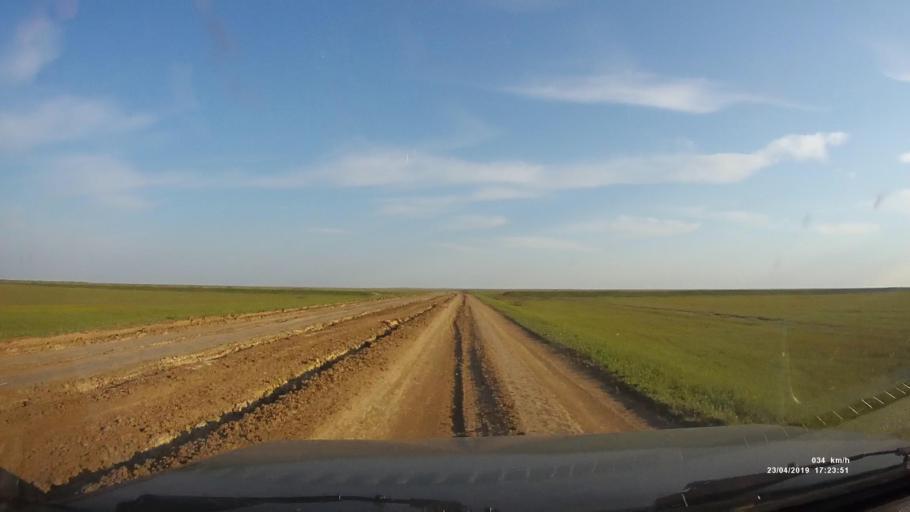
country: RU
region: Kalmykiya
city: Priyutnoye
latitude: 46.1599
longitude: 43.5080
